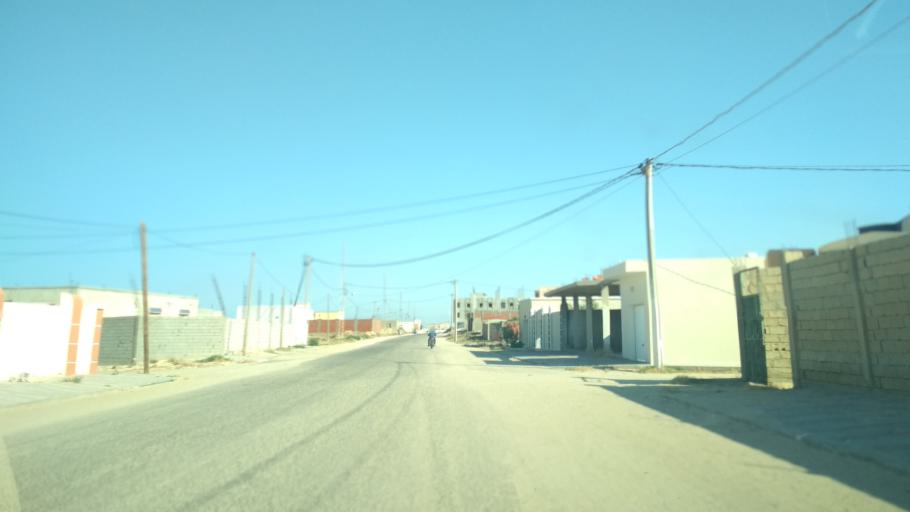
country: TN
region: Qabis
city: Gabes
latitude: 33.9567
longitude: 10.0638
